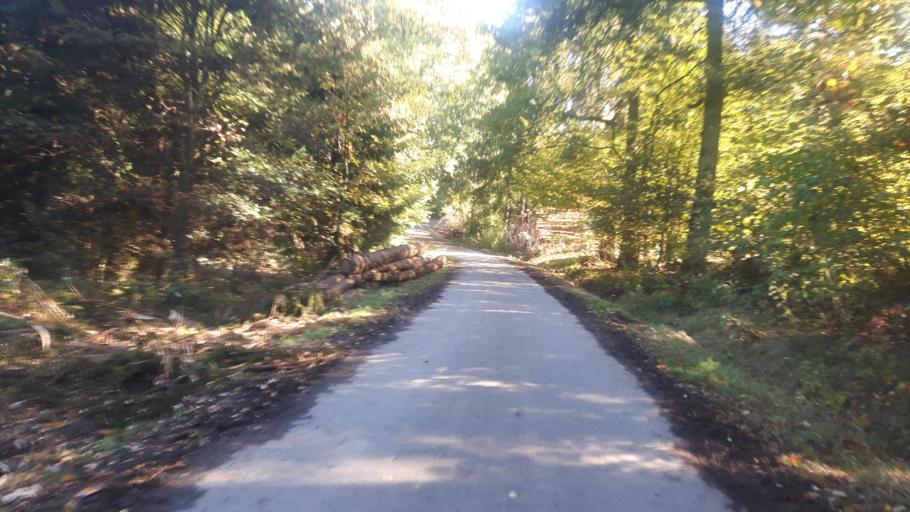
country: DE
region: Rheinland-Pfalz
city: Niederirsen
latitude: 50.7993
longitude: 7.5882
